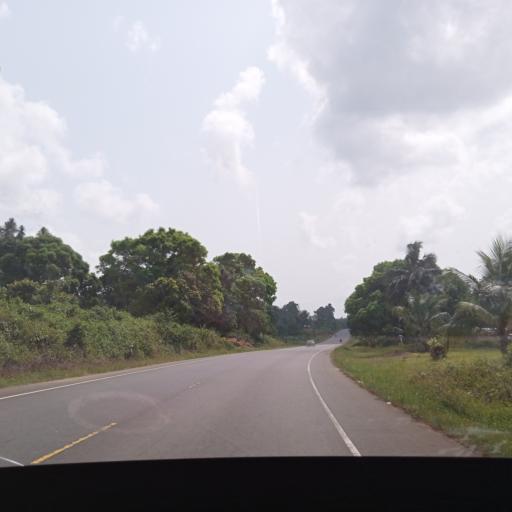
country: LR
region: Margibi
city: Kakata
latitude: 6.2495
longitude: -10.2953
